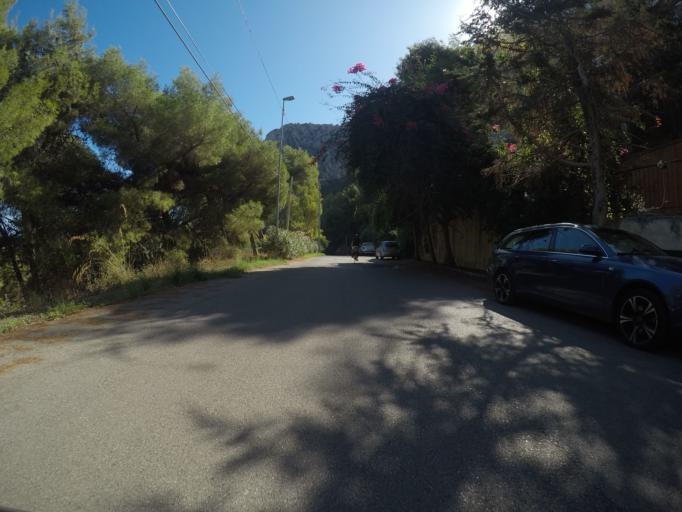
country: IT
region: Sicily
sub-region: Palermo
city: Palermo
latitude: 38.1871
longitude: 13.3451
